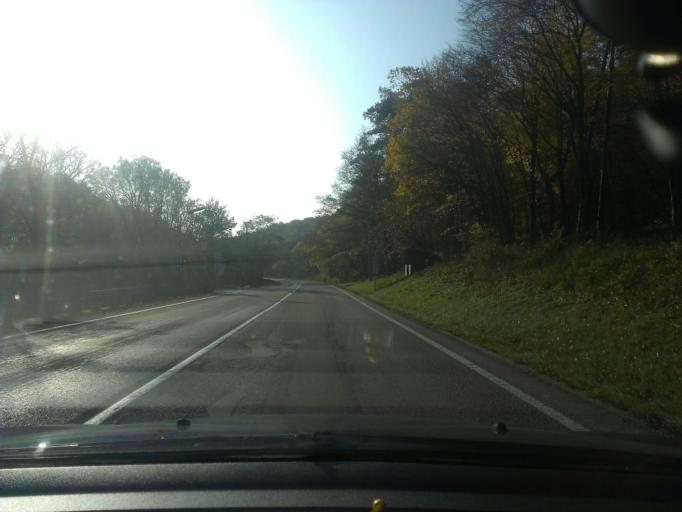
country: SK
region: Trnavsky
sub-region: Okres Trnava
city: Piestany
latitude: 48.5586
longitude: 17.9146
